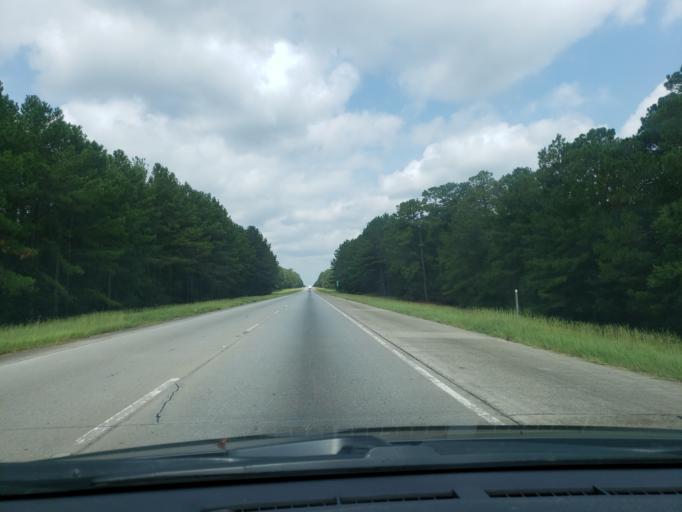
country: US
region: Georgia
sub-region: Emanuel County
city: Swainsboro
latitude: 32.4095
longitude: -82.3536
